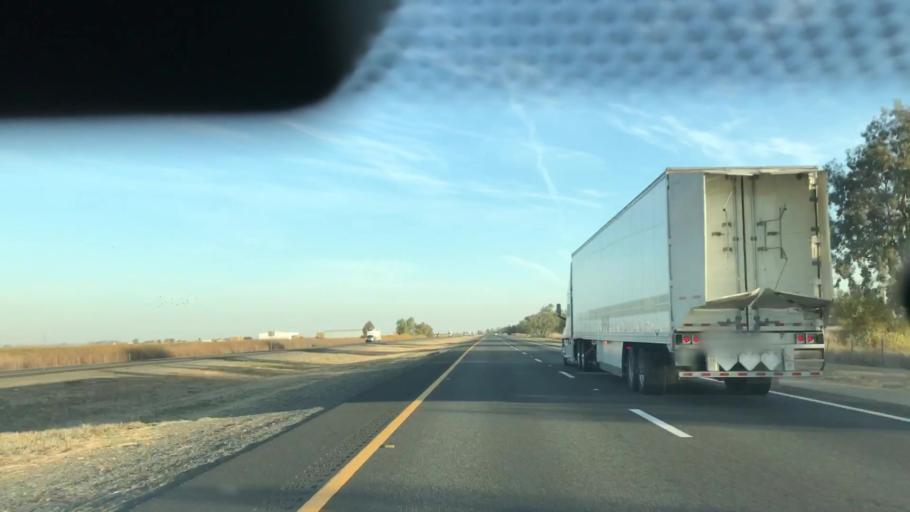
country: US
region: California
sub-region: Colusa County
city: Maxwell
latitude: 39.3786
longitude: -122.1929
